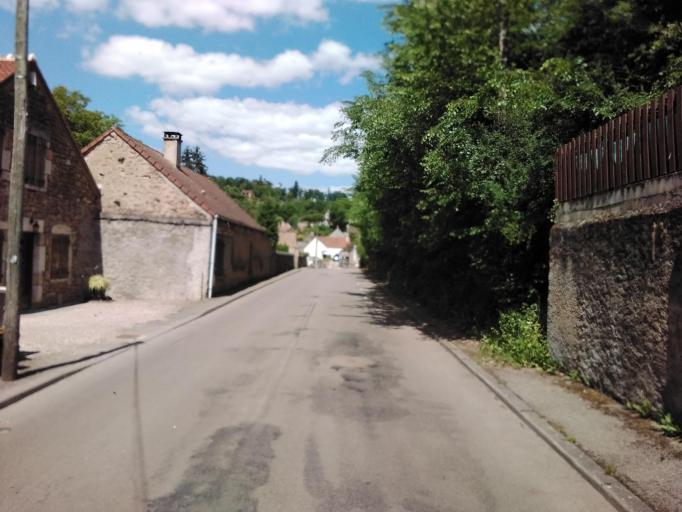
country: FR
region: Bourgogne
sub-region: Departement de l'Yonne
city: Avallon
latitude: 47.4808
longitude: 3.9095
